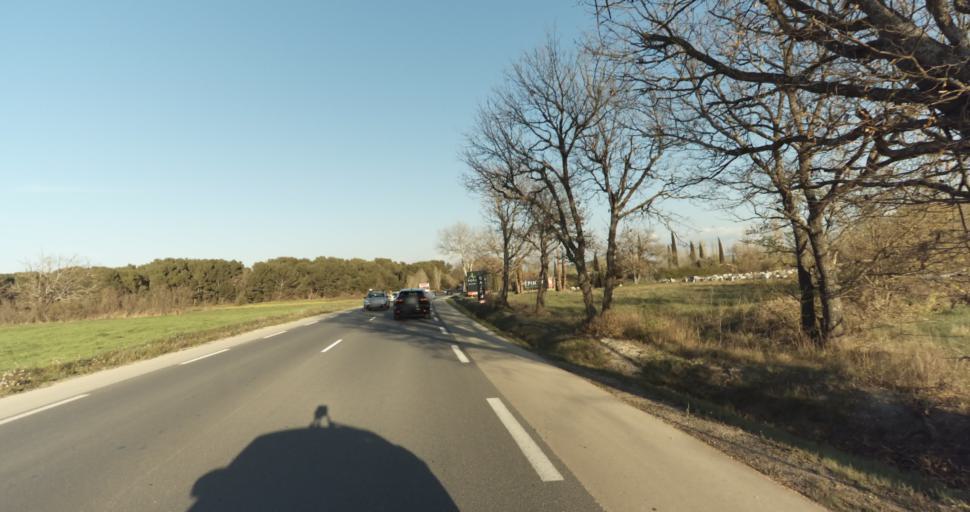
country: FR
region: Provence-Alpes-Cote d'Azur
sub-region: Departement des Bouches-du-Rhone
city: Eguilles
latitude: 43.5458
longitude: 5.3374
